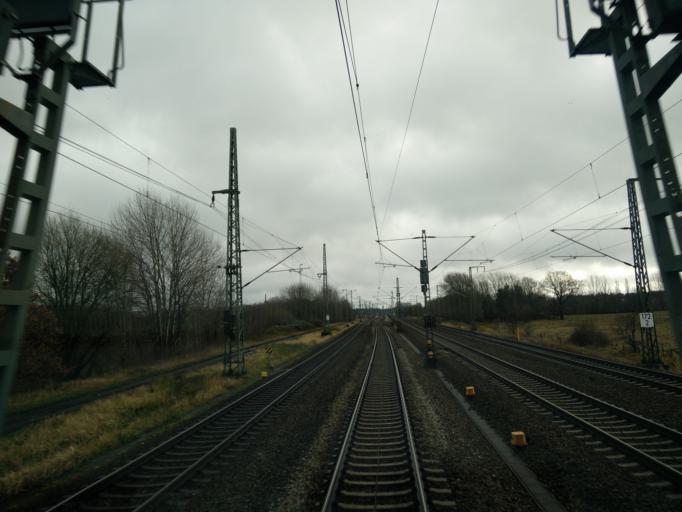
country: DE
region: Mecklenburg-Vorpommern
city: Ludwigslust
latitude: 53.3429
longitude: 11.4774
